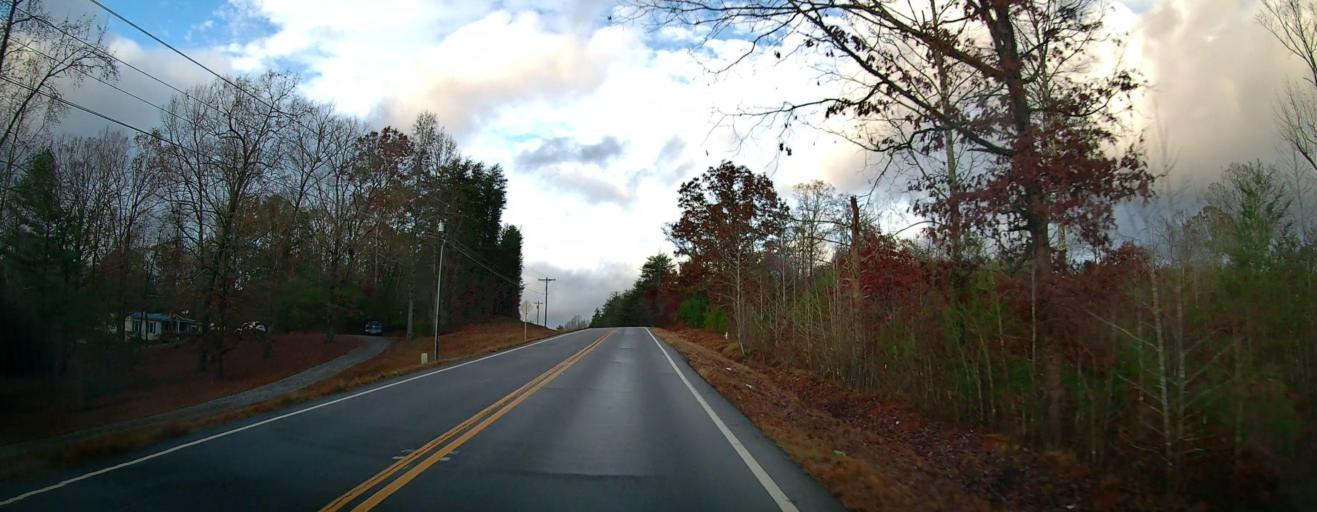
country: US
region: Georgia
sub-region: White County
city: Cleveland
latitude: 34.6310
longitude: -83.7992
